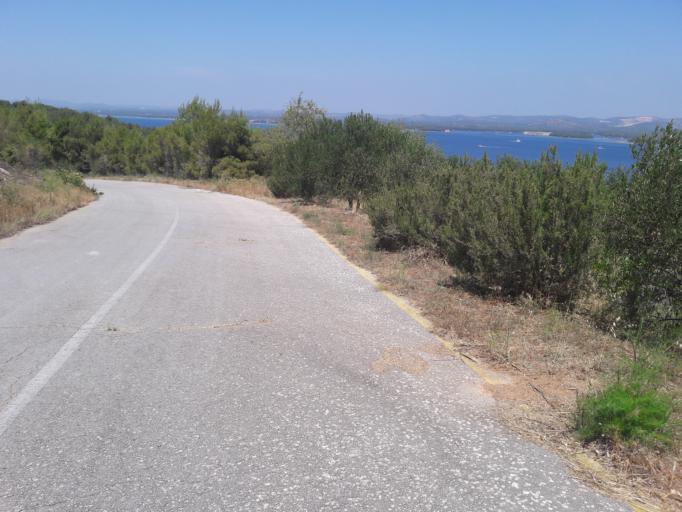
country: HR
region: Sibensko-Kniniska
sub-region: Grad Sibenik
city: Sibenik
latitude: 43.6996
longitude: 15.8479
